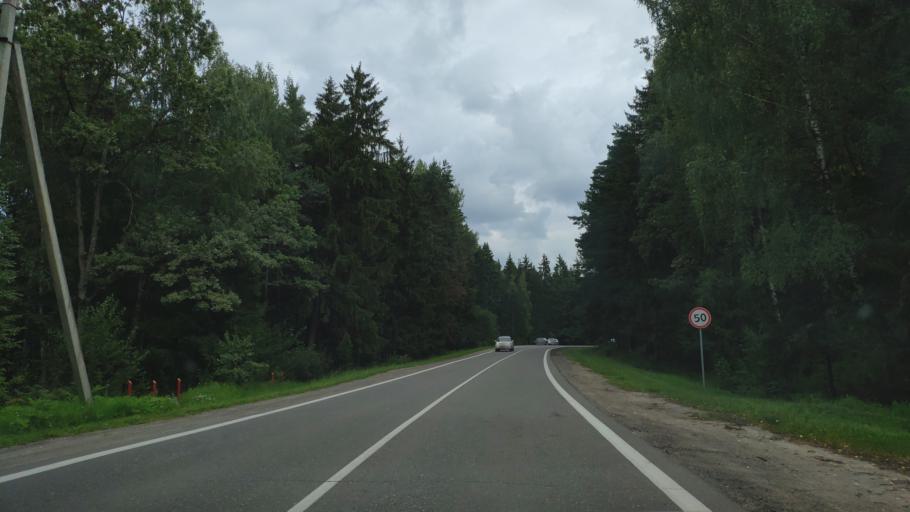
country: BY
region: Minsk
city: Syomkava
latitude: 53.9887
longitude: 27.4595
